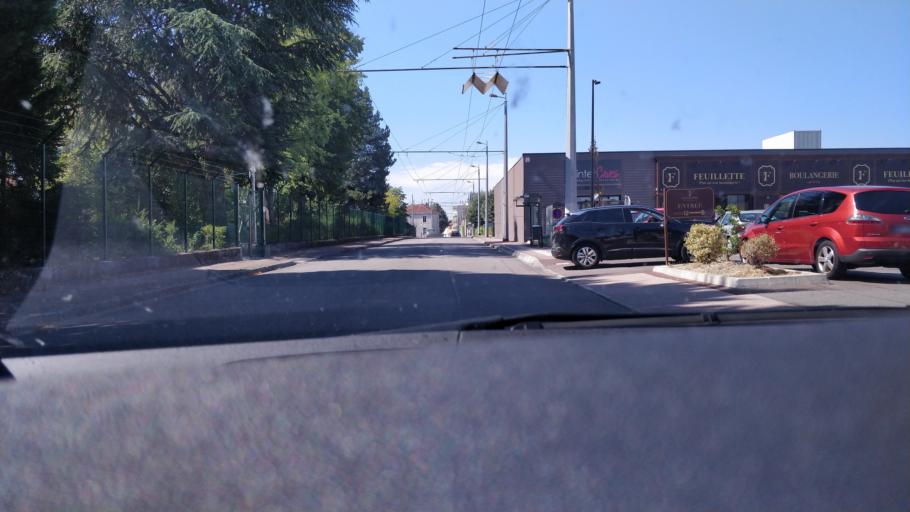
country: FR
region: Limousin
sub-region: Departement de la Haute-Vienne
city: Limoges
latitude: 45.8521
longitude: 1.2545
